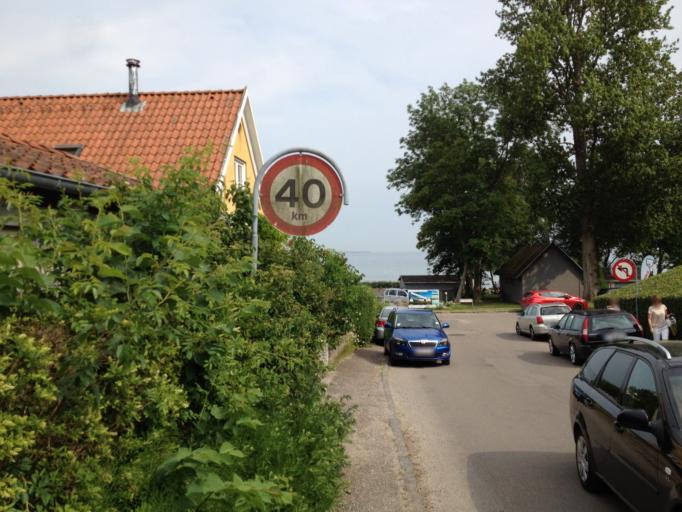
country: DK
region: Capital Region
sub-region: Fredensborg Kommune
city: Humlebaek
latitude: 55.9516
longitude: 12.5316
